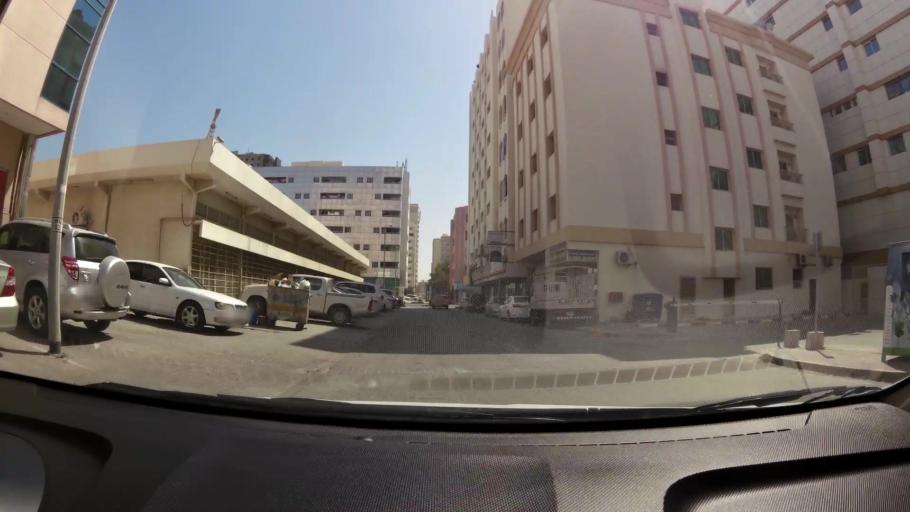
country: AE
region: Ajman
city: Ajman
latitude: 25.4039
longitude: 55.4409
